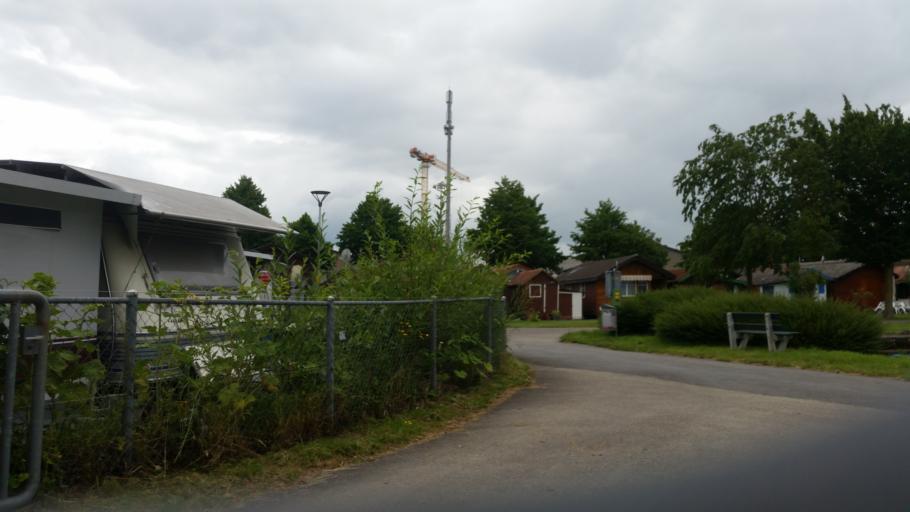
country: CH
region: Vaud
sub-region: Jura-Nord vaudois District
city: Yverdon-les-Bains
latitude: 46.7852
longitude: 6.6487
